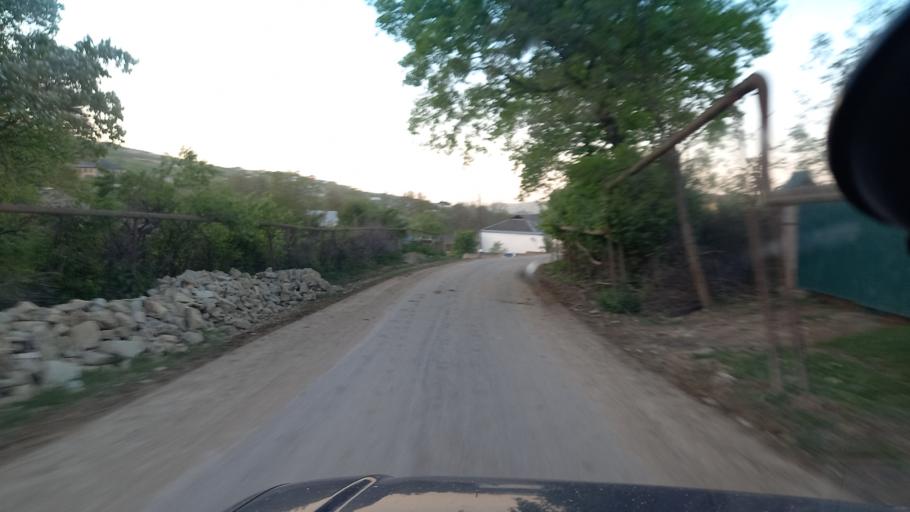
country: RU
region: Dagestan
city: Khuchni
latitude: 42.0273
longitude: 47.9668
